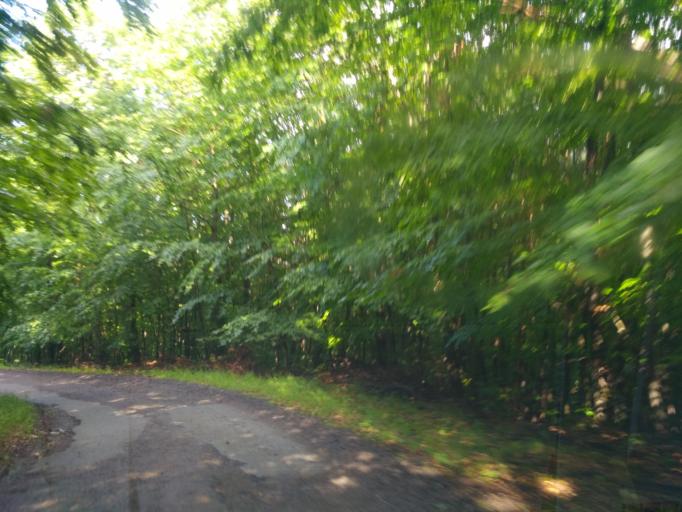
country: SK
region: Kosicky
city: Secovce
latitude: 48.6004
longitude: 21.5130
